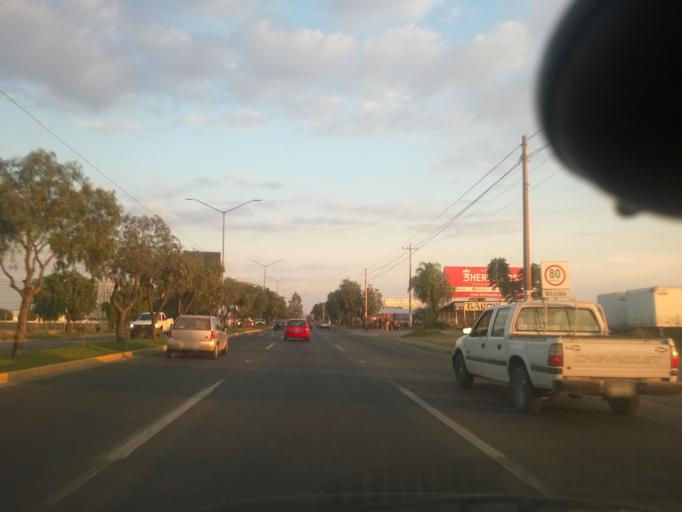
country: MX
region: Guanajuato
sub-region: Leon
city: Fraccionamiento Paraiso Real
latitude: 21.0780
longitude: -101.6055
